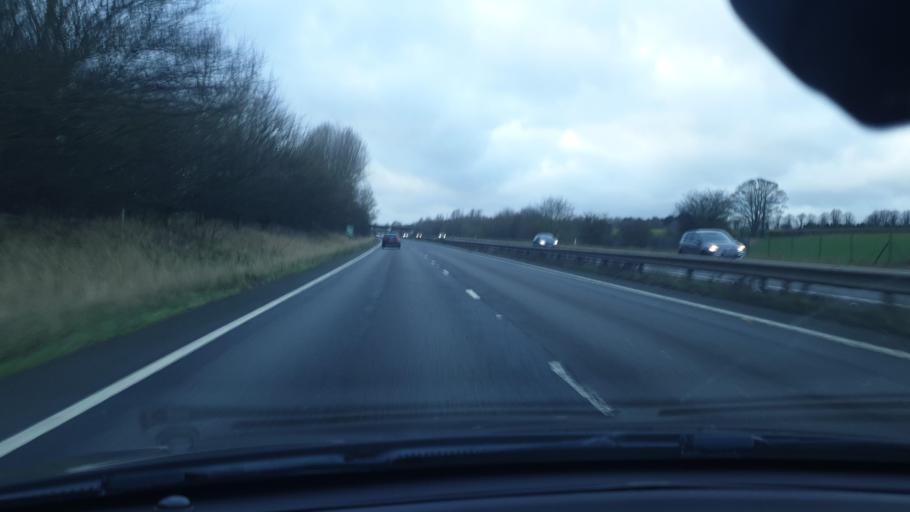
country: GB
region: England
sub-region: Northamptonshire
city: Long Buckby
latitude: 52.3981
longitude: -1.0243
